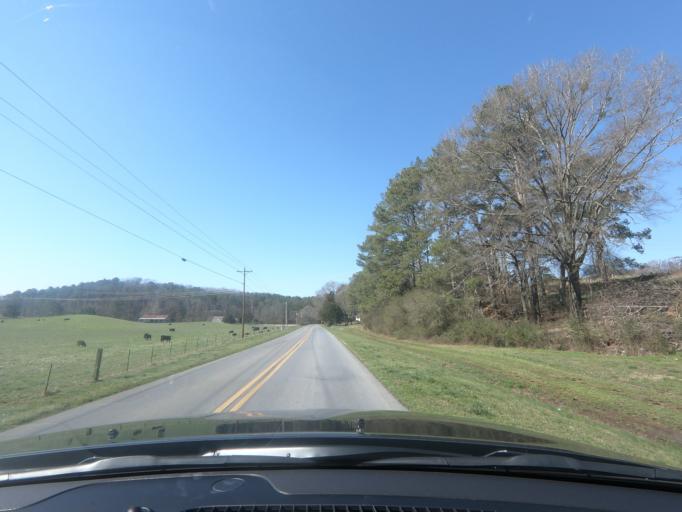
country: US
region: Georgia
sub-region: Gordon County
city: Calhoun
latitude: 34.4616
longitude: -84.9934
